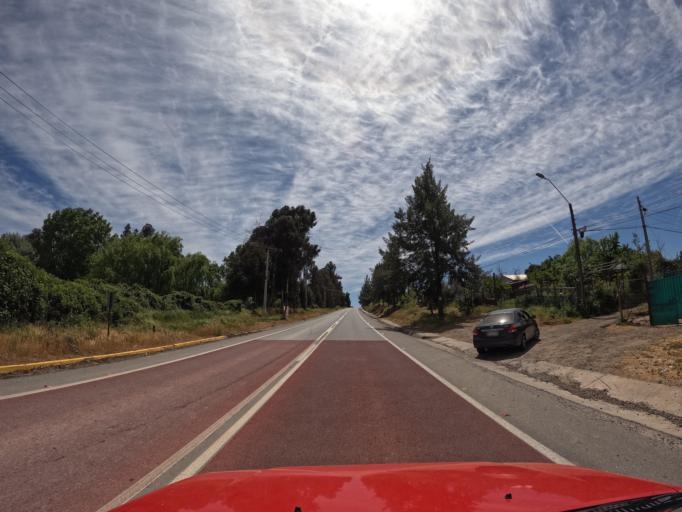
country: CL
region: Maule
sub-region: Provincia de Talca
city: Talca
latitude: -35.3009
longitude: -71.5240
